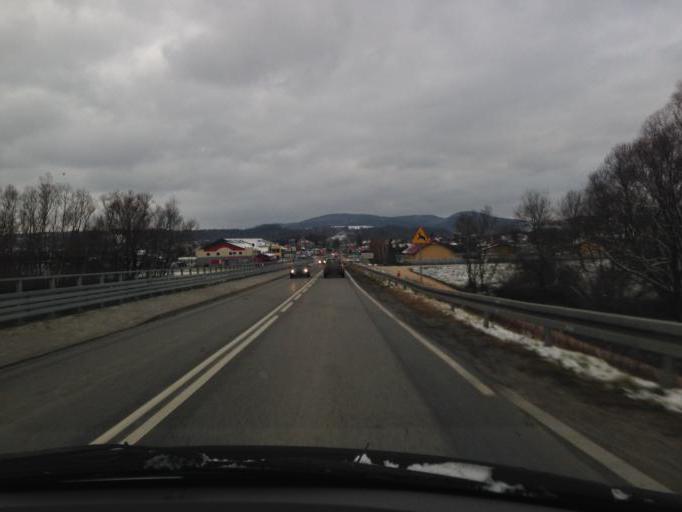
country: PL
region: Lesser Poland Voivodeship
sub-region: Powiat tarnowski
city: Zakliczyn
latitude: 49.8637
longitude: 20.8128
